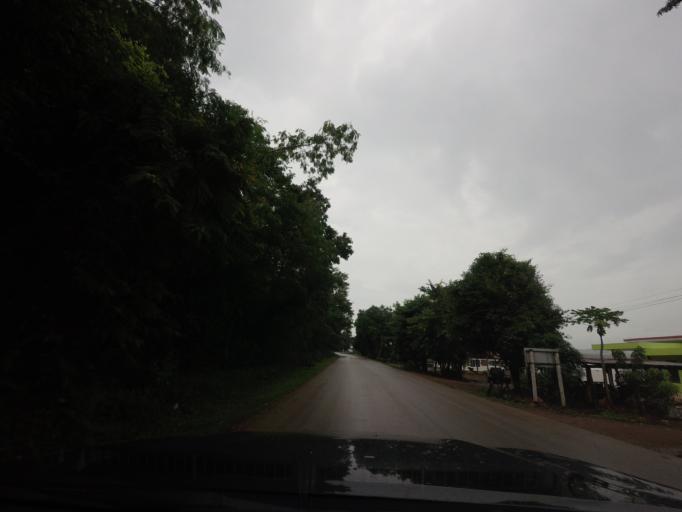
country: TH
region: Loei
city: Pak Chom
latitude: 18.1105
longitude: 101.9818
